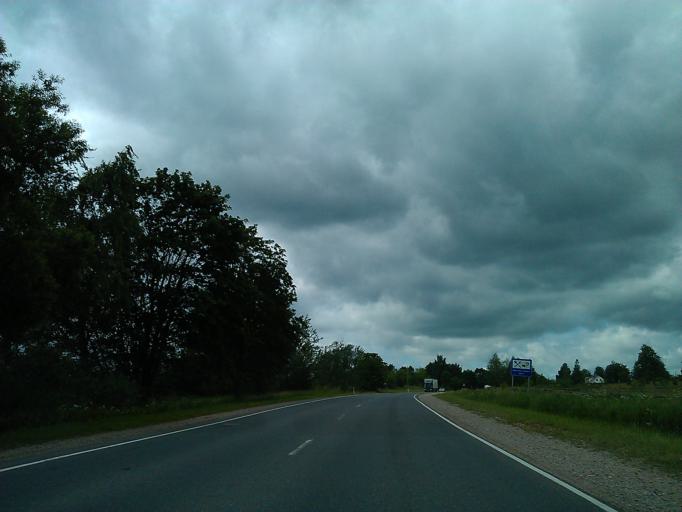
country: LV
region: Engure
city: Smarde
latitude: 56.9200
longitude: 23.2699
